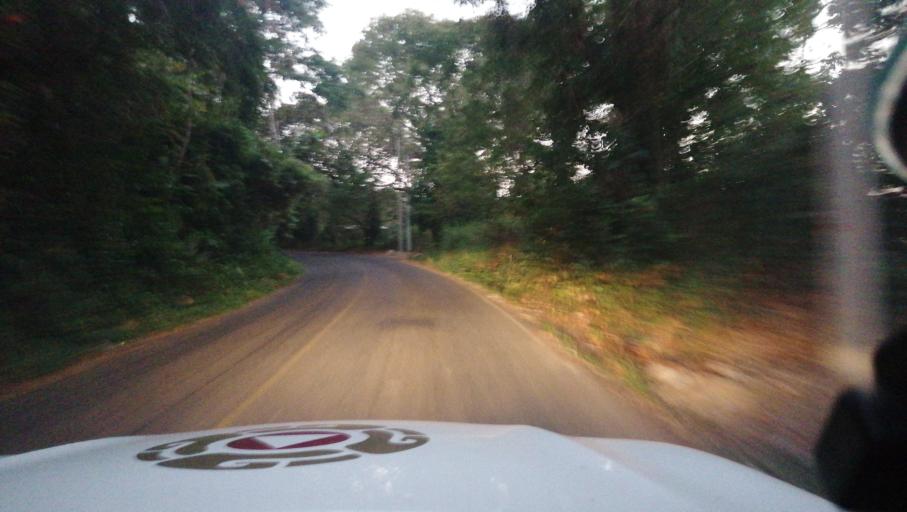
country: MX
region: Chiapas
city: Veinte de Noviembre
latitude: 14.9897
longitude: -92.2423
